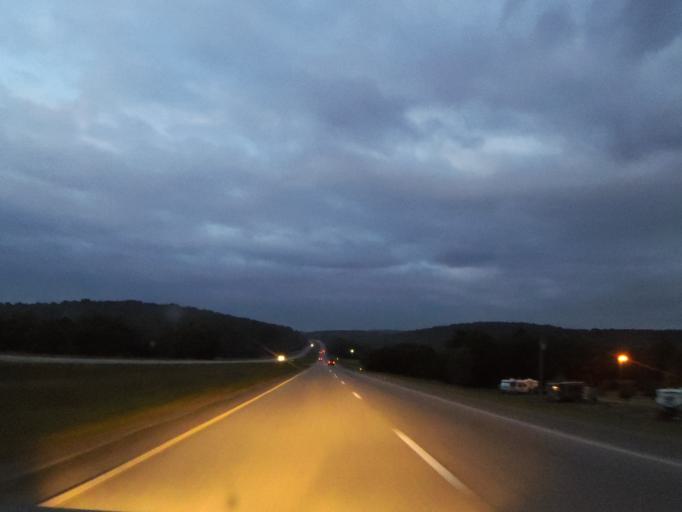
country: US
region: Alabama
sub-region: Madison County
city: New Hope
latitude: 34.6145
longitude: -86.2346
